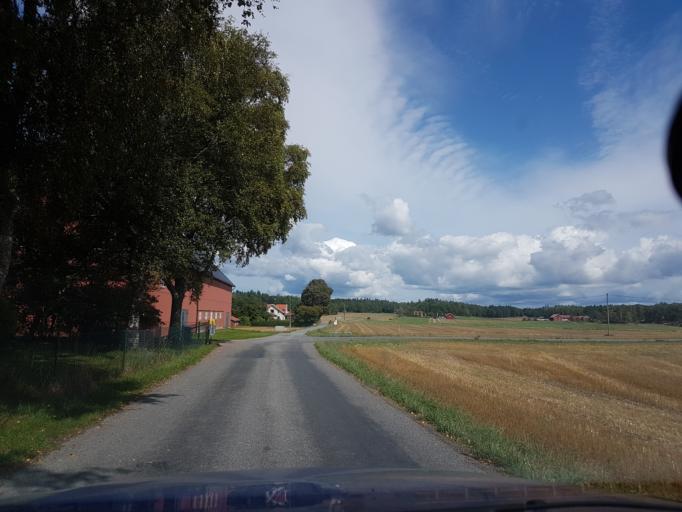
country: SE
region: Vaestra Goetaland
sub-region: Lerums Kommun
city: Grabo
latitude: 57.8461
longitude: 12.3305
